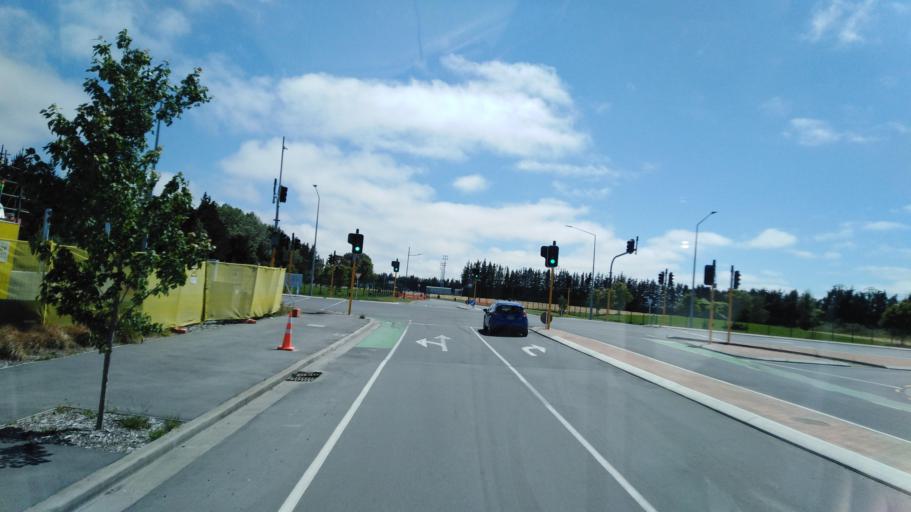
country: NZ
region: Canterbury
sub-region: Selwyn District
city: Prebbleton
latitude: -43.5183
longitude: 172.5261
